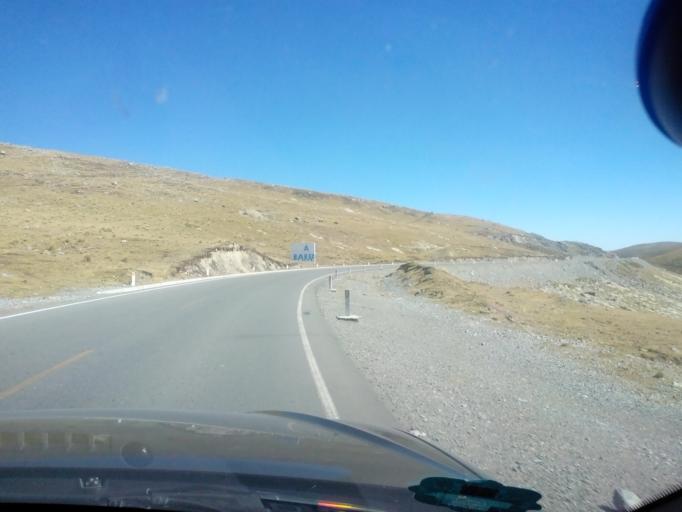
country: PE
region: Apurimac
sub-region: Chincheros
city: Ranracancha
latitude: -13.6080
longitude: -73.5718
